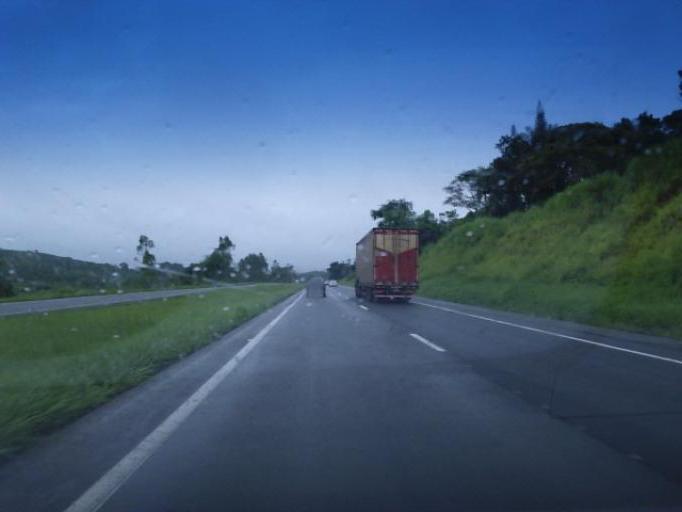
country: BR
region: Sao Paulo
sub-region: Registro
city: Registro
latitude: -24.4216
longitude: -47.7744
